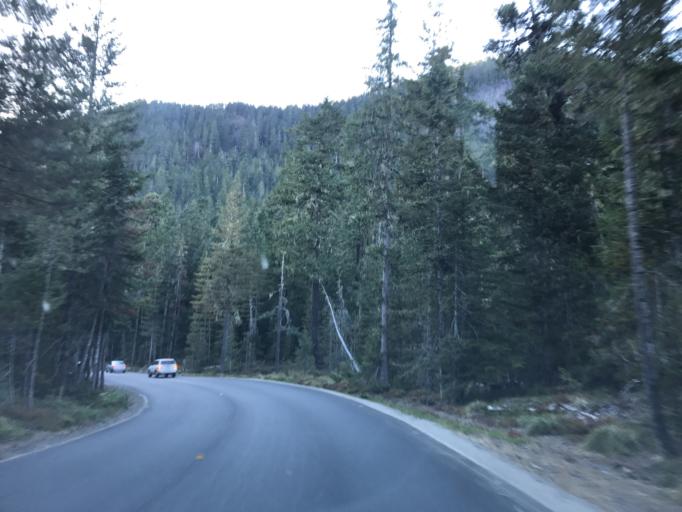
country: US
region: Washington
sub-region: Pierce County
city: Buckley
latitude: 46.7710
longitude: -121.7884
